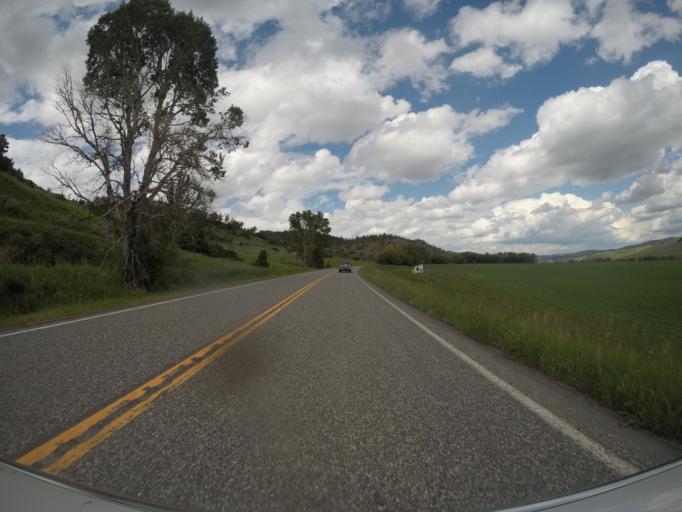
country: US
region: Montana
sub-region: Sweet Grass County
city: Big Timber
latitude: 45.6826
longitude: -110.0848
